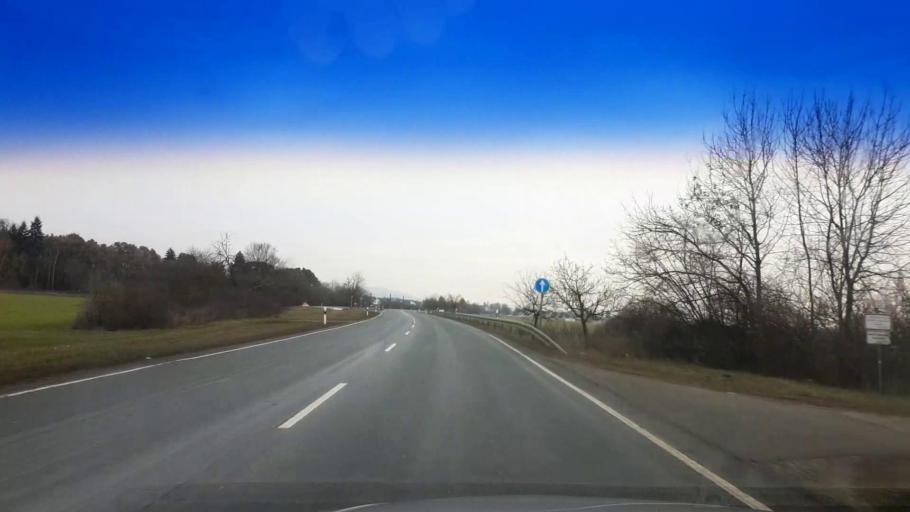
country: DE
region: Bavaria
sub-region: Upper Franconia
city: Hirschaid
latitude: 49.8083
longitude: 11.0015
